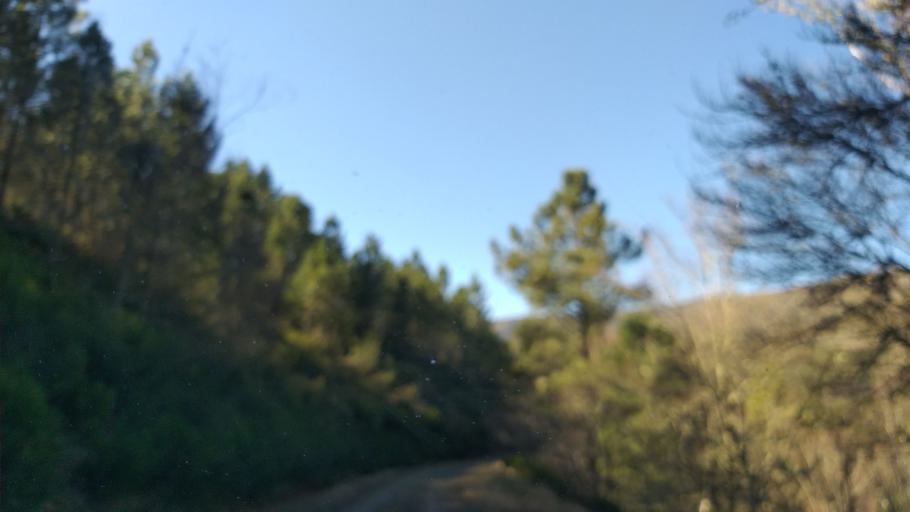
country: PT
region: Guarda
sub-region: Manteigas
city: Manteigas
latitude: 40.4425
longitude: -7.5083
